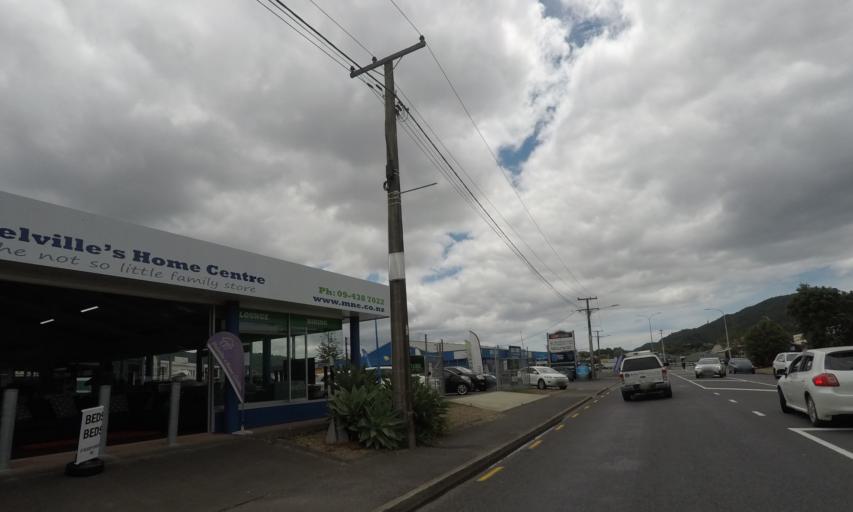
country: NZ
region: Northland
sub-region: Whangarei
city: Whangarei
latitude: -35.7307
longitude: 174.3266
